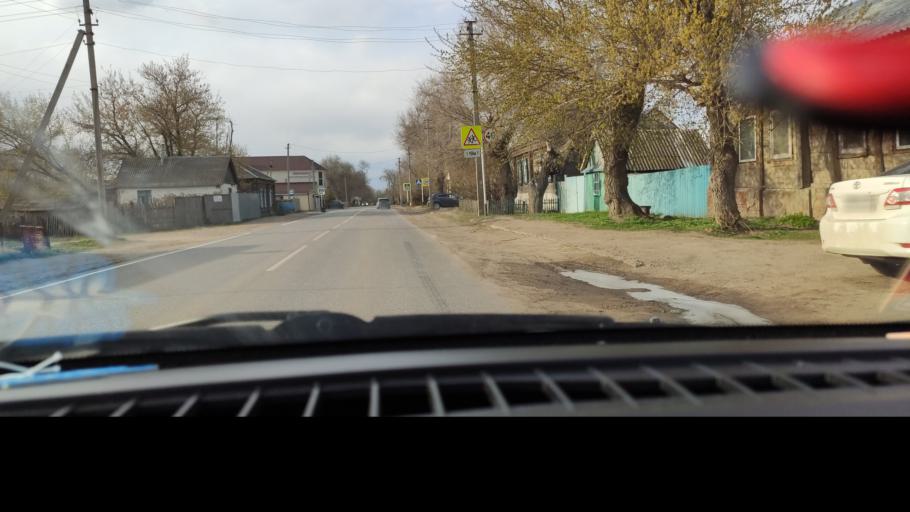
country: RU
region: Saratov
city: Privolzhskiy
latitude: 51.1858
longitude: 45.9174
